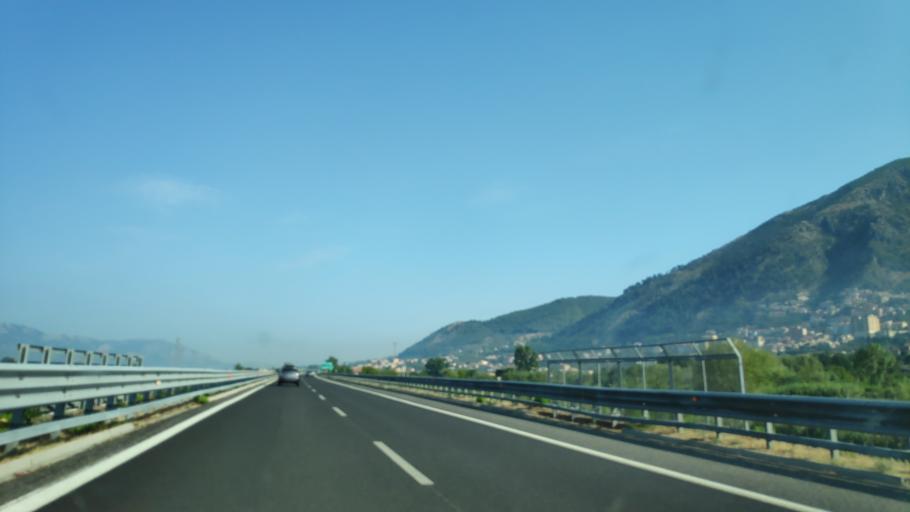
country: IT
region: Campania
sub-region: Provincia di Salerno
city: Sala Consilina
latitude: 40.3906
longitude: 15.5867
